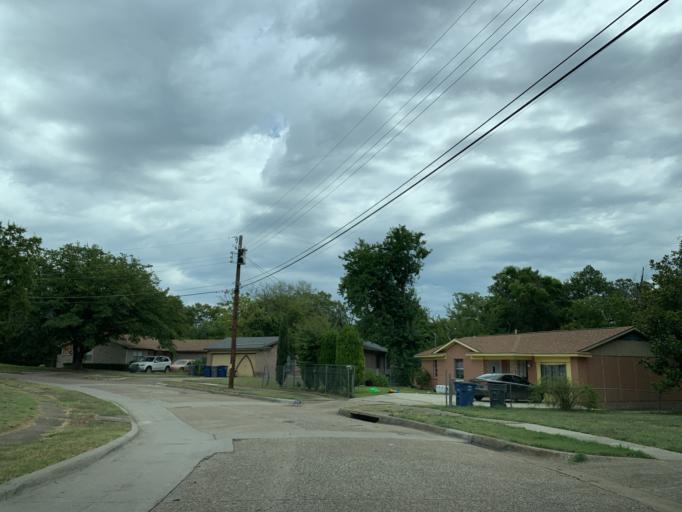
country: US
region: Texas
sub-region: Dallas County
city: DeSoto
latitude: 32.6574
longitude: -96.8257
